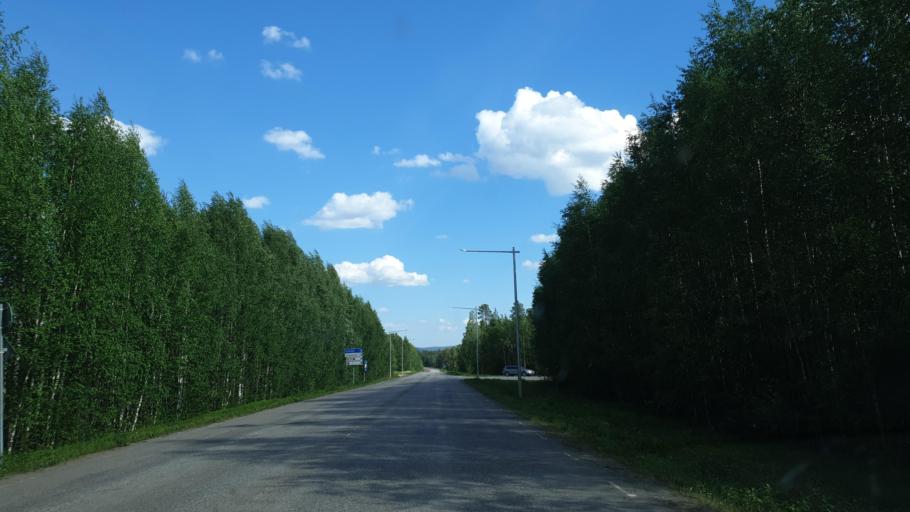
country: SE
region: Norrbotten
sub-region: Alvsbyns Kommun
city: AElvsbyn
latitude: 65.8401
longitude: 20.5067
